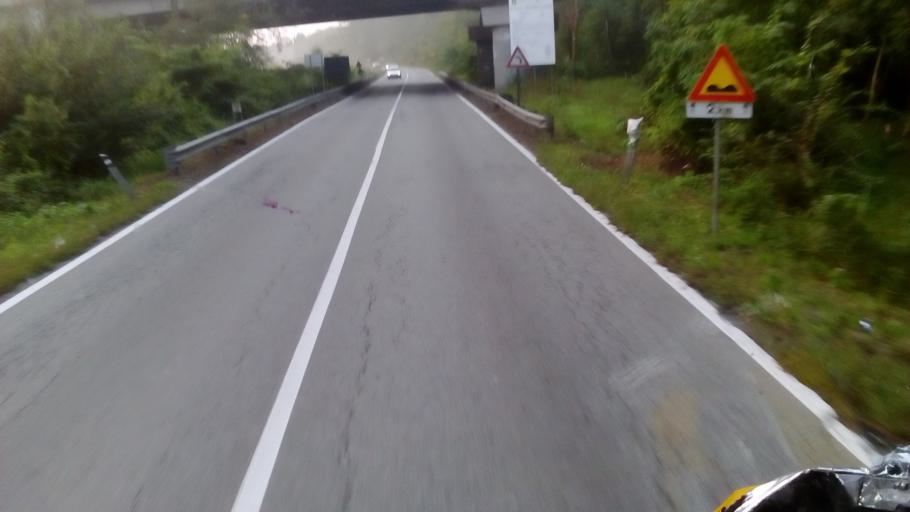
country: IT
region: Piedmont
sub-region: Provincia di Novara
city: Borgo Ticino
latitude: 45.7042
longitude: 8.5878
